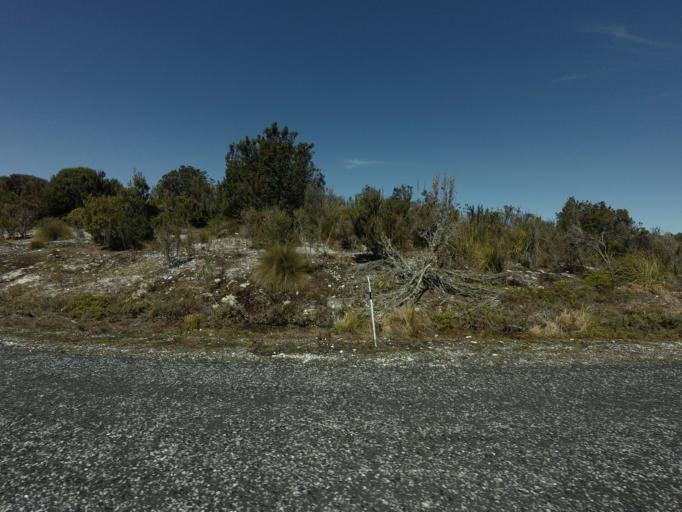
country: AU
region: Tasmania
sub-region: Huon Valley
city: Geeveston
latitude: -42.8355
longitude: 146.1339
